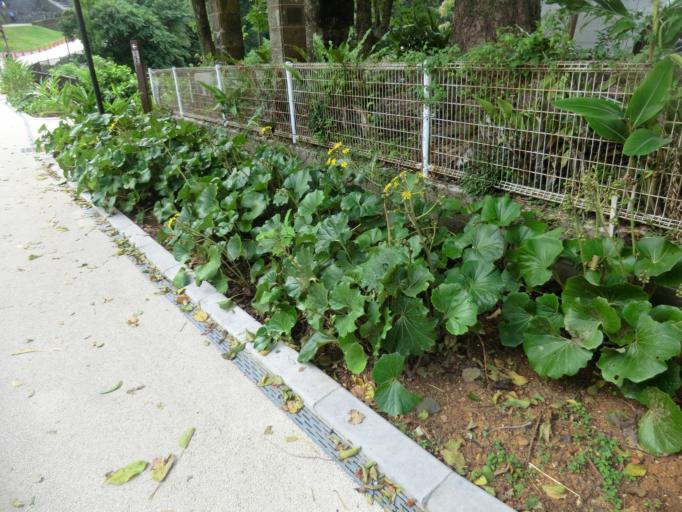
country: JP
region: Okinawa
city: Naha-shi
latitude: 26.2162
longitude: 127.7194
